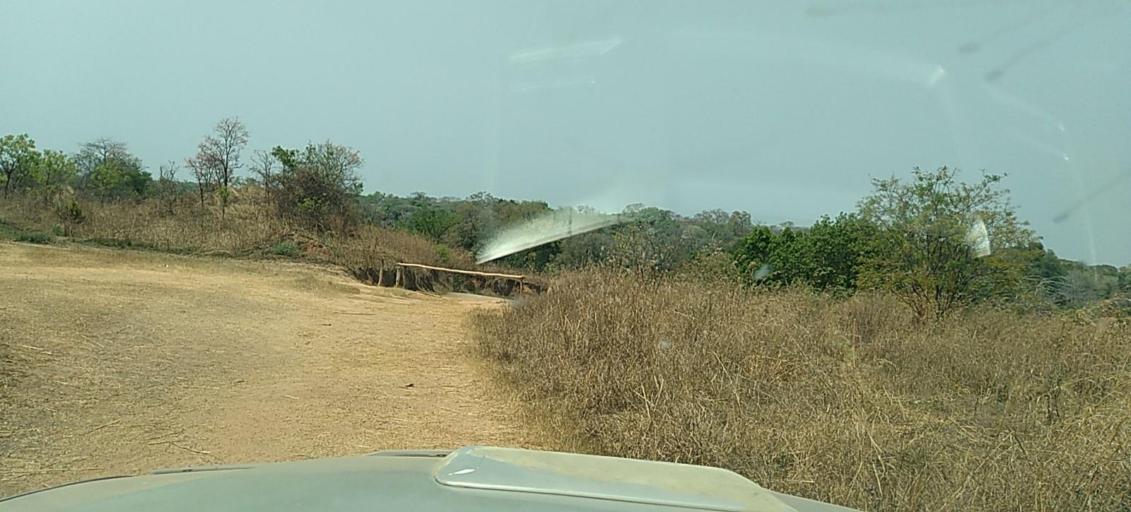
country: ZM
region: North-Western
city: Kasempa
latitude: -13.7112
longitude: 26.3394
